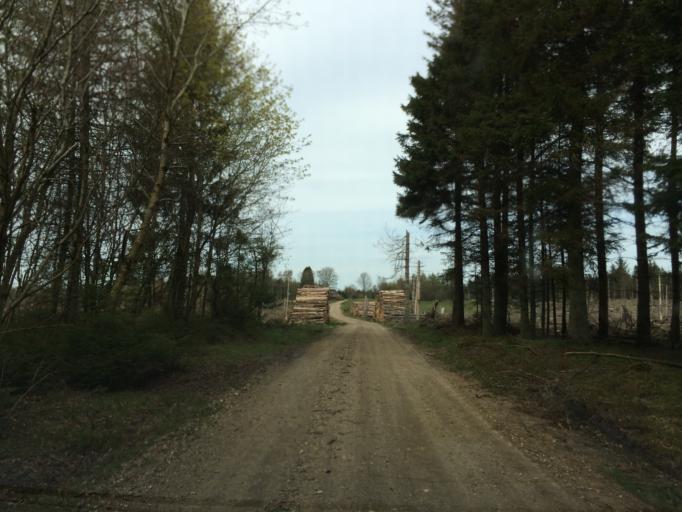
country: DK
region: Central Jutland
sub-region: Holstebro Kommune
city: Ulfborg
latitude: 56.2334
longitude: 8.4736
